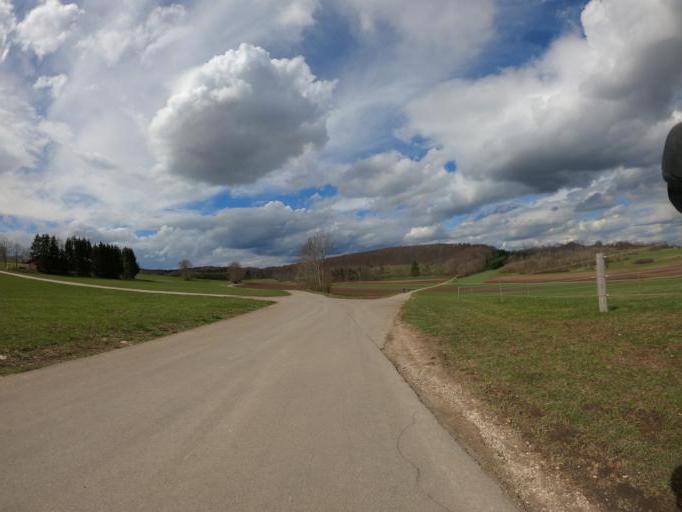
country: DE
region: Baden-Wuerttemberg
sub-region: Tuebingen Region
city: Pfullingen
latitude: 48.3984
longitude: 9.1711
